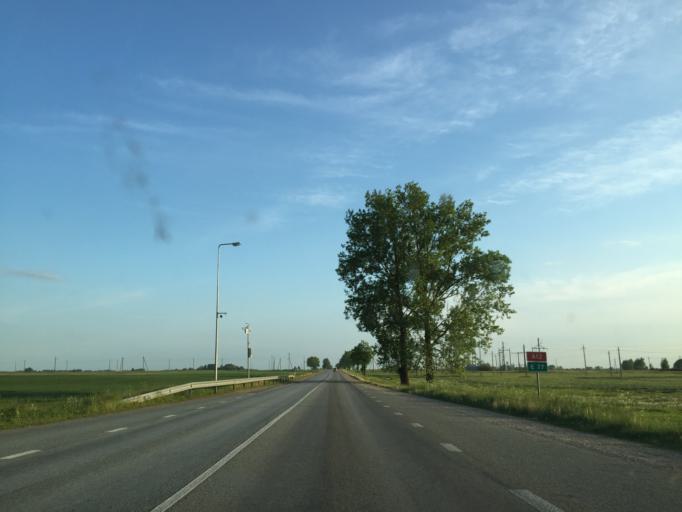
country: LT
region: Siauliu apskritis
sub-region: Siauliai
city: Siauliai
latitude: 56.0748
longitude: 23.4548
